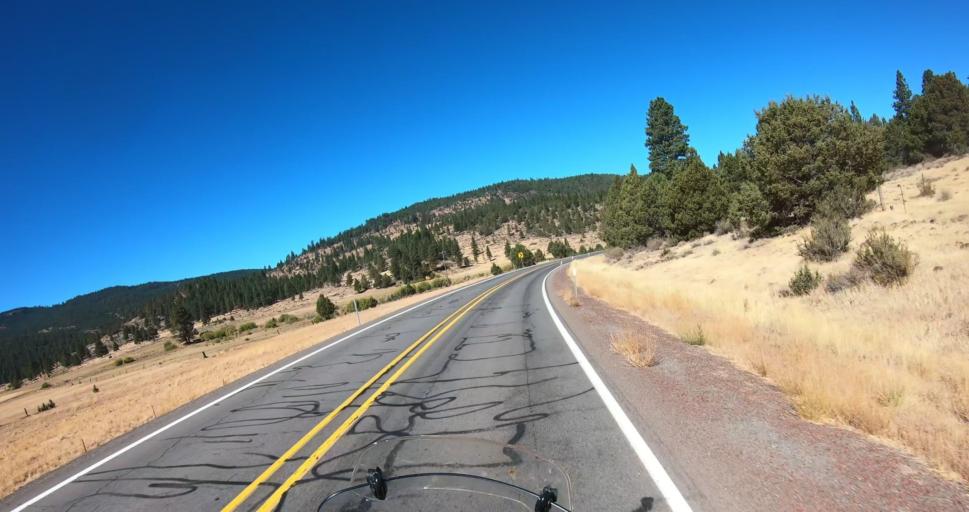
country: US
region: Oregon
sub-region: Lake County
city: Lakeview
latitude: 42.3834
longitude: -120.3064
